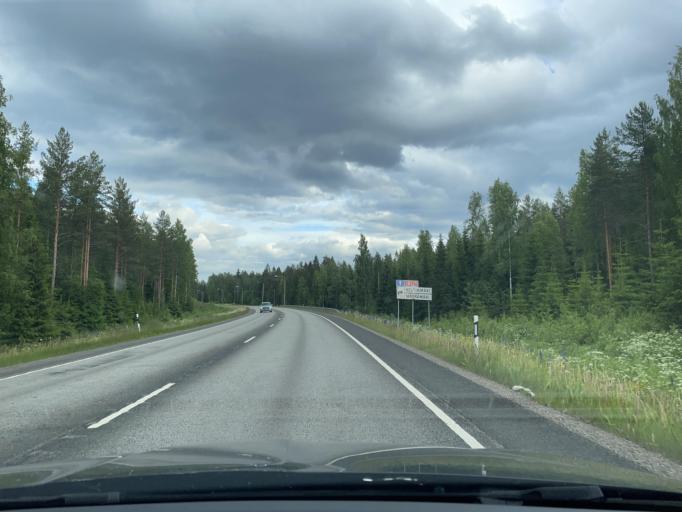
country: FI
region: Central Finland
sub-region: Jyvaeskylae
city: Jyvaeskylae
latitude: 62.2366
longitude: 25.6639
